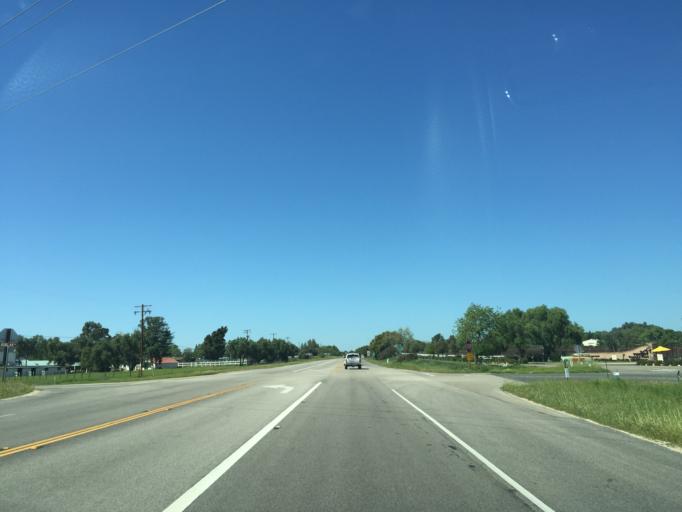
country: US
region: California
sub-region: Santa Barbara County
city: Los Olivos
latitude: 34.6503
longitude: -120.0950
